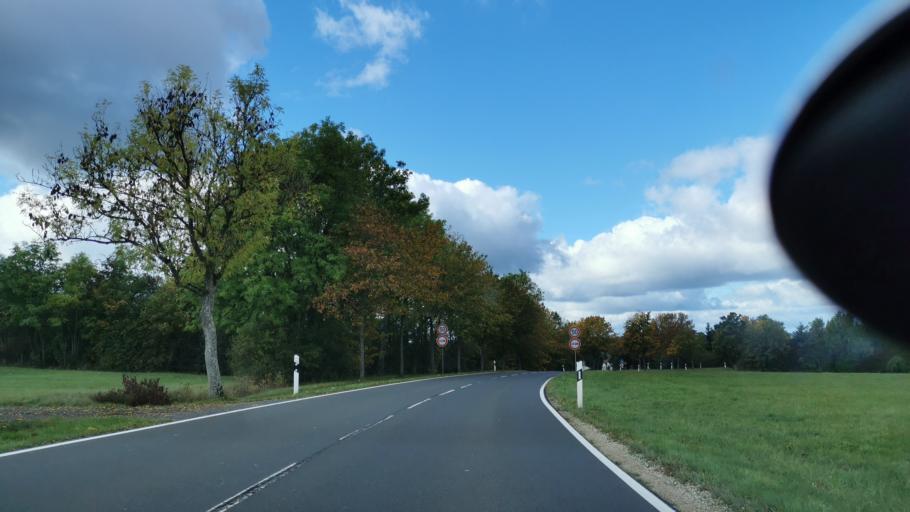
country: DE
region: Rheinland-Pfalz
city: Walsdorf
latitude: 50.2796
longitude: 6.7205
